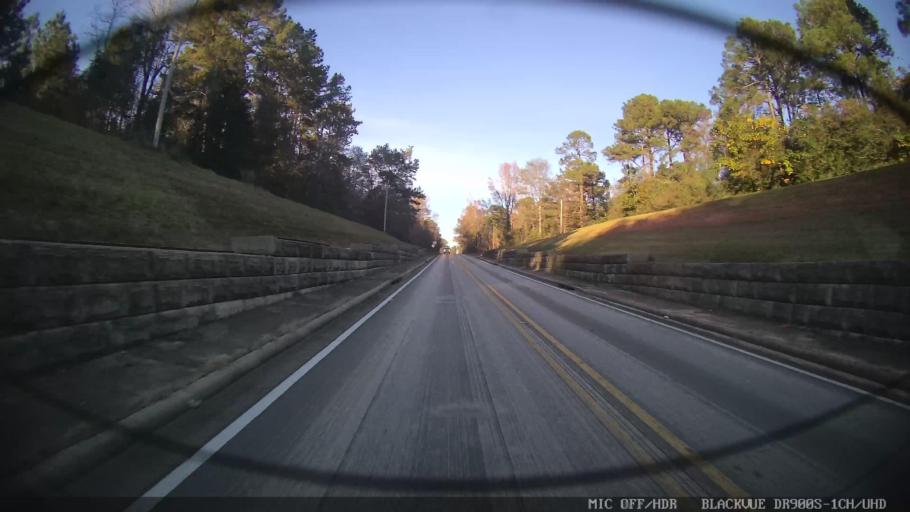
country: US
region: Mississippi
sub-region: Lamar County
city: Lumberton
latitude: 31.0288
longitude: -89.4455
